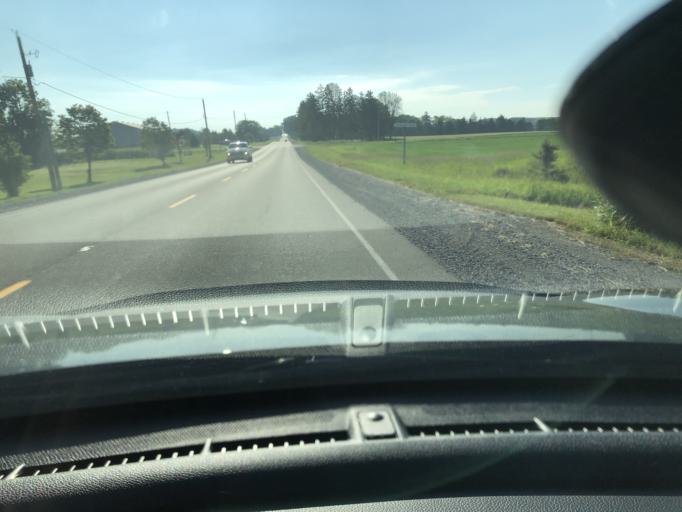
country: CA
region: Ontario
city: Stratford
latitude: 43.4248
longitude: -80.8152
